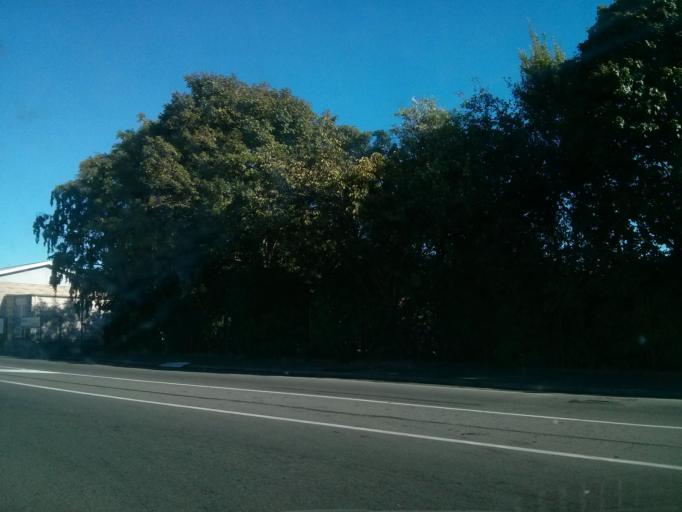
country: NZ
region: Canterbury
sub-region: Christchurch City
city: Christchurch
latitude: -43.5303
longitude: 172.5930
